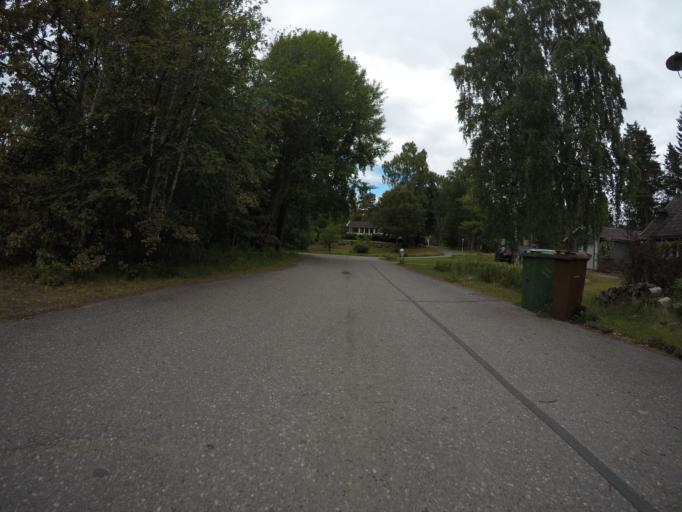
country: SE
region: Soedermanland
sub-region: Eskilstuna Kommun
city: Kvicksund
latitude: 59.4635
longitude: 16.3231
